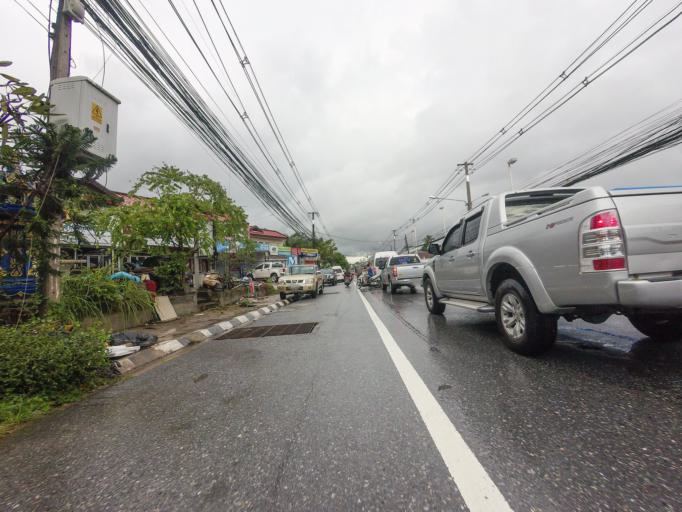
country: TH
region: Surat Thani
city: Ko Samui
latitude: 9.5191
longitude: 100.0490
